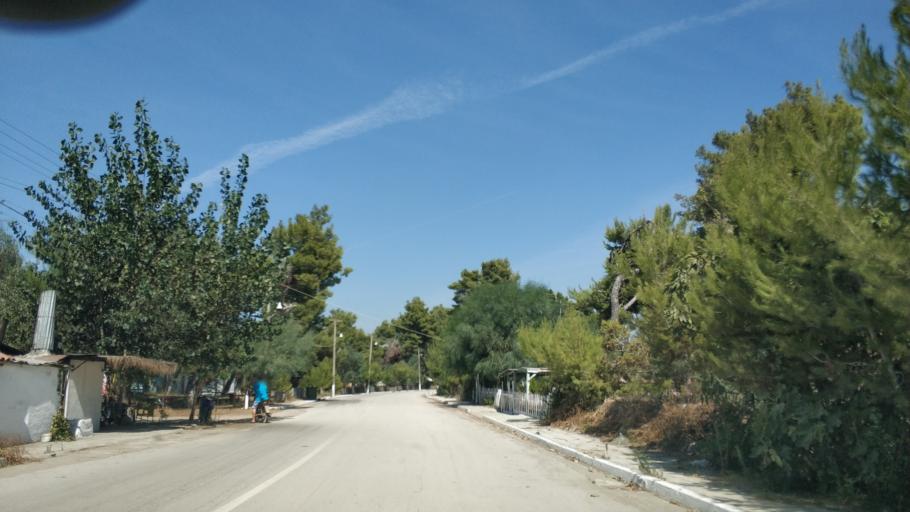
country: AL
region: Fier
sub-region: Rrethi i Lushnjes
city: Divjake
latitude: 40.9674
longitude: 19.4786
